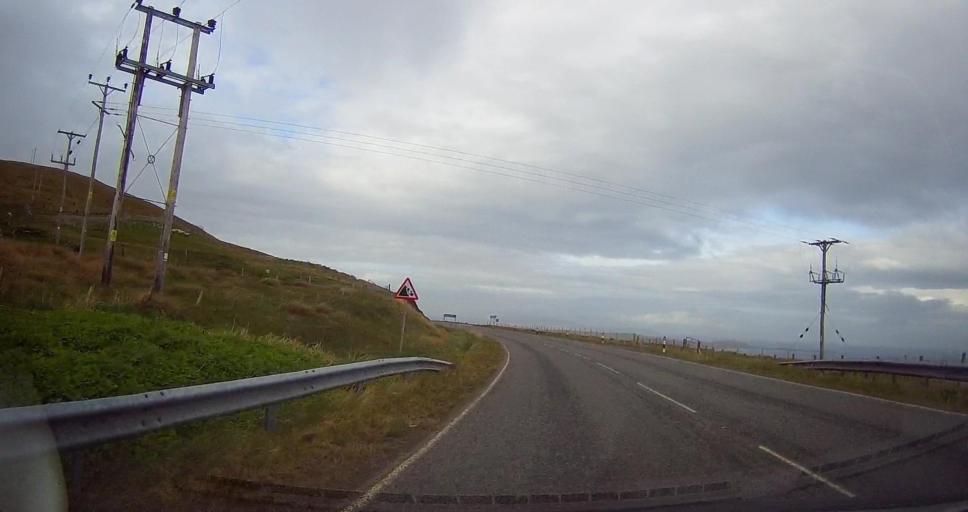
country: GB
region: Scotland
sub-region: Shetland Islands
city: Sandwick
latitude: 60.0162
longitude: -1.2327
